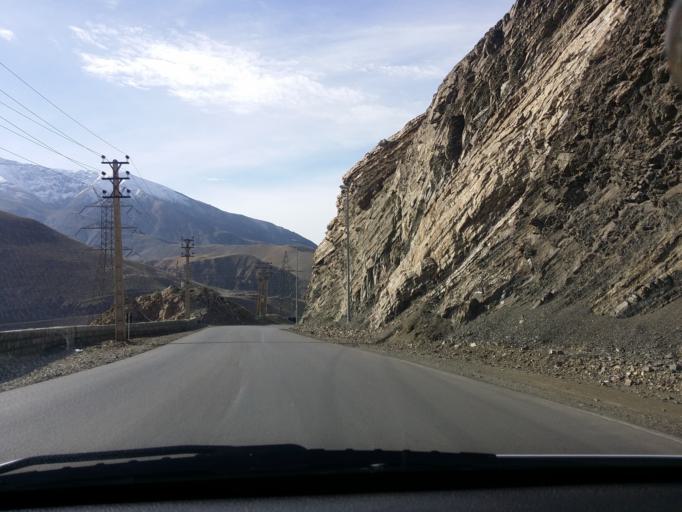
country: IR
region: Alborz
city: Karaj
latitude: 35.9475
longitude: 51.0832
